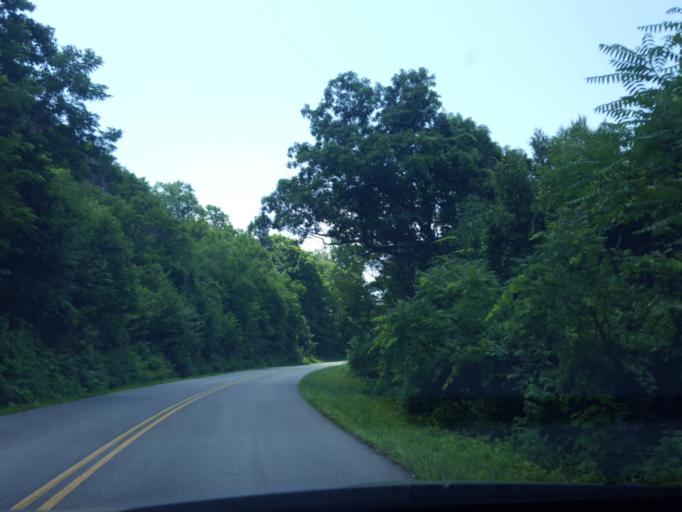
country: US
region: Virginia
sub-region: Nelson County
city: Nellysford
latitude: 37.9108
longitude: -78.9745
